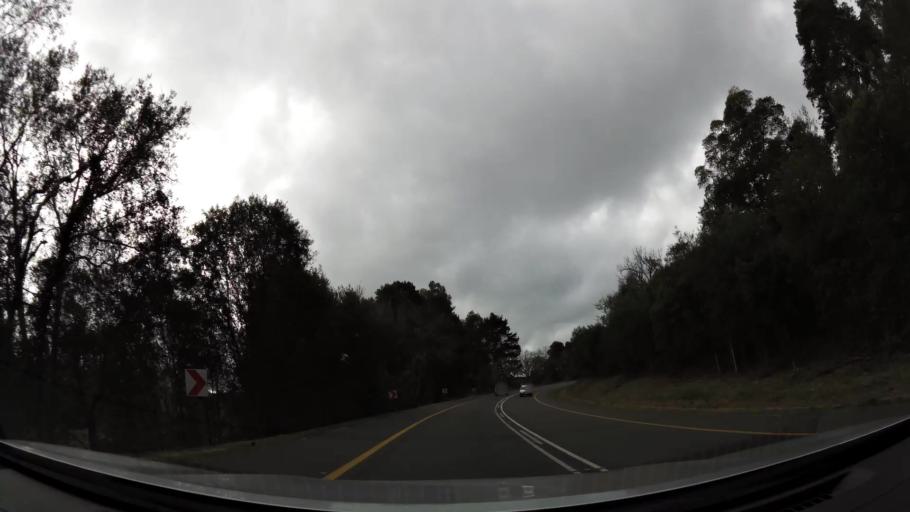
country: ZA
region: Western Cape
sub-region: Eden District Municipality
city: Knysna
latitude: -34.0265
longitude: 23.1596
